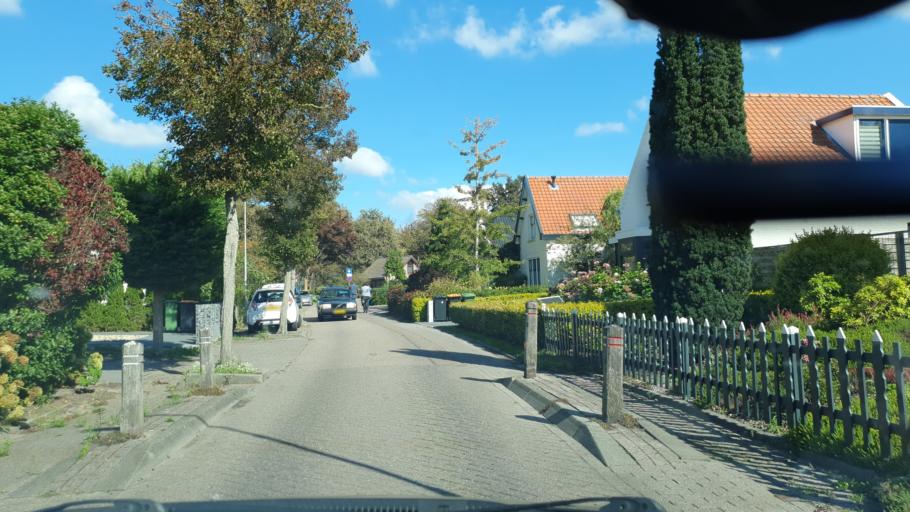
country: NL
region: Zeeland
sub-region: Schouwen-Duiveland
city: Burgh
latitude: 51.6888
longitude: 3.7361
